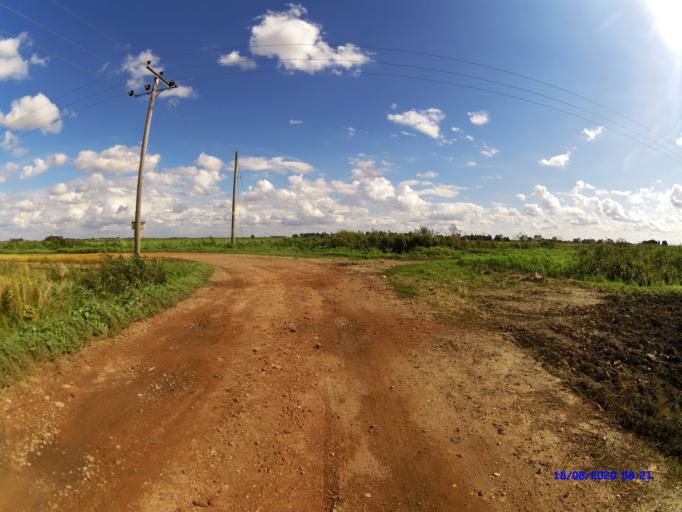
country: GB
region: England
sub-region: Cambridgeshire
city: Ramsey
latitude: 52.5038
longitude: -0.0754
